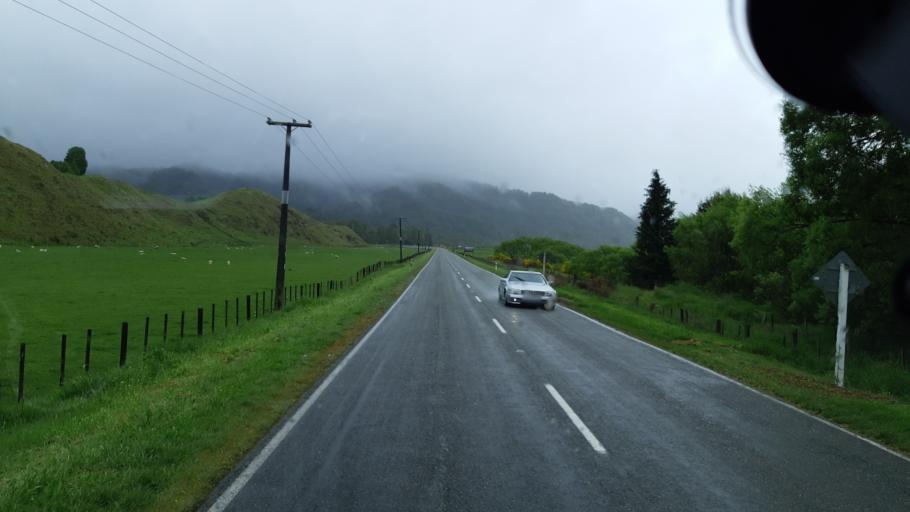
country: NZ
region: West Coast
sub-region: Buller District
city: Westport
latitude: -42.1221
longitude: 171.8533
